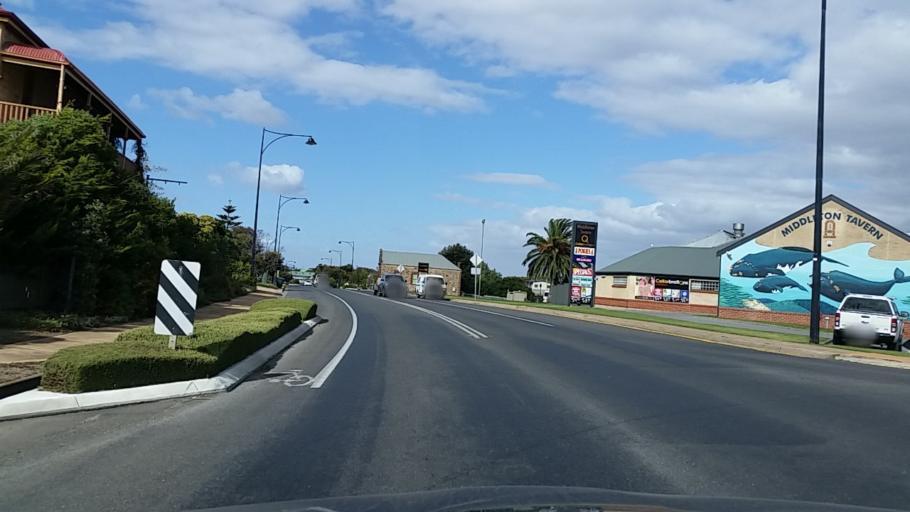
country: AU
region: South Australia
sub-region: Alexandrina
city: Port Elliot
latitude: -35.5107
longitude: 138.7051
